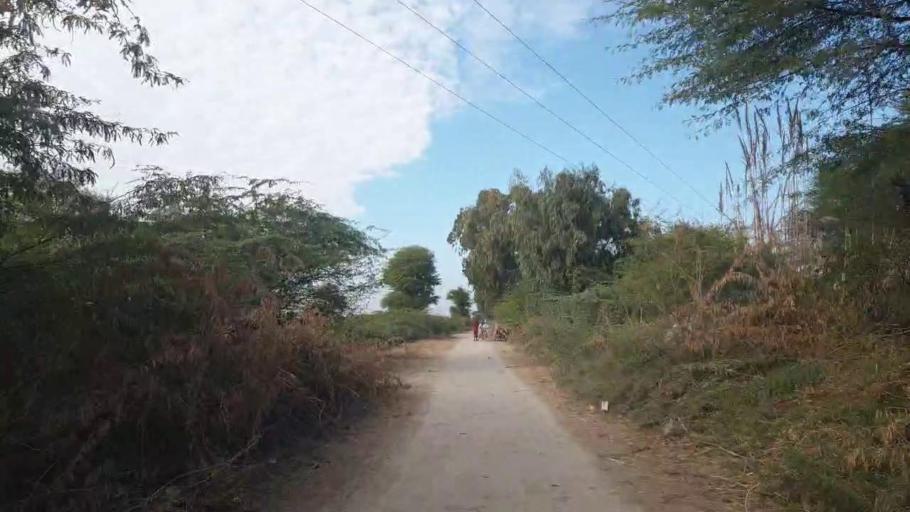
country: PK
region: Sindh
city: Sinjhoro
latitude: 26.0414
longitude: 68.8772
